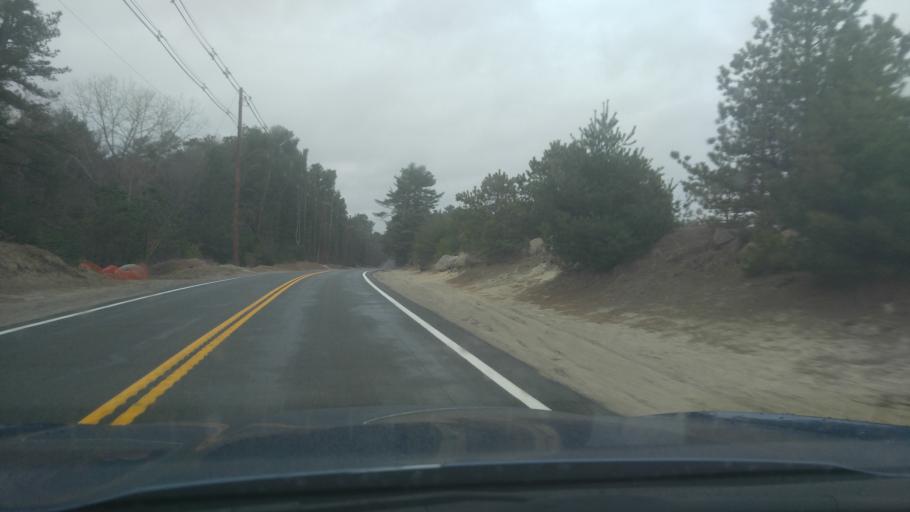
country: US
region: Rhode Island
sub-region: Kent County
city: West Greenwich
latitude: 41.6467
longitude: -71.5874
